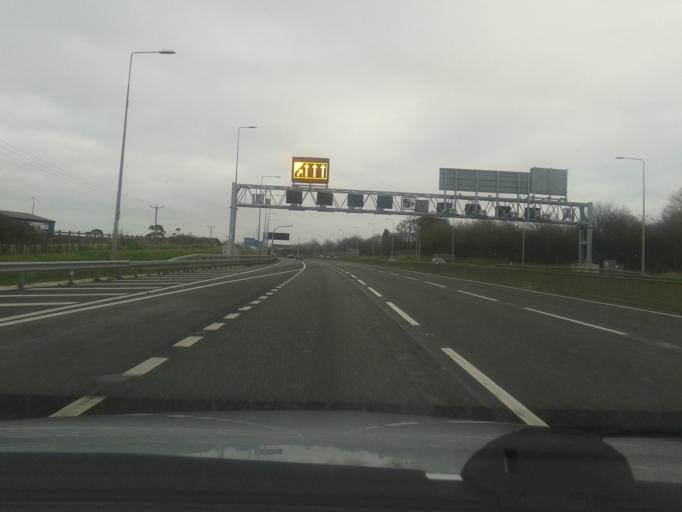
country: GB
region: England
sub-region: South Gloucestershire
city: Almondsbury
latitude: 51.5325
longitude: -2.5958
